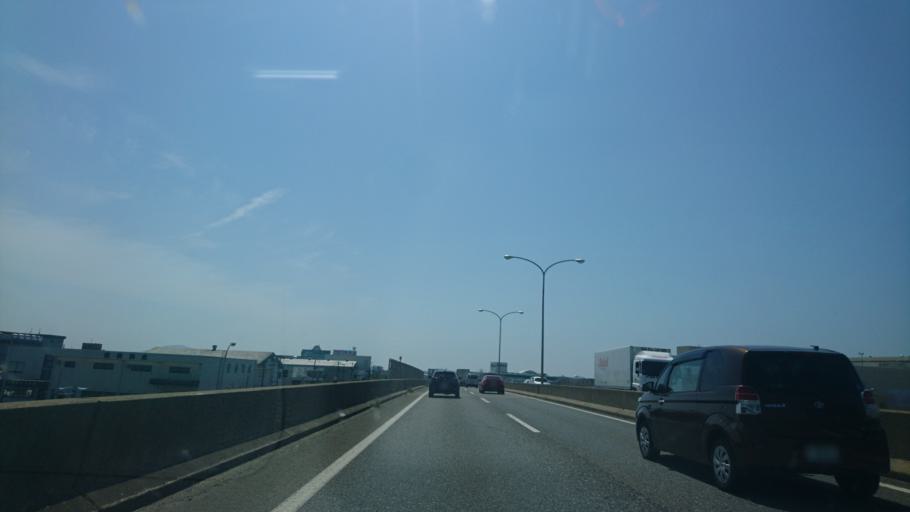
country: JP
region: Niigata
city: Niigata-shi
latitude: 37.8673
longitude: 138.9973
